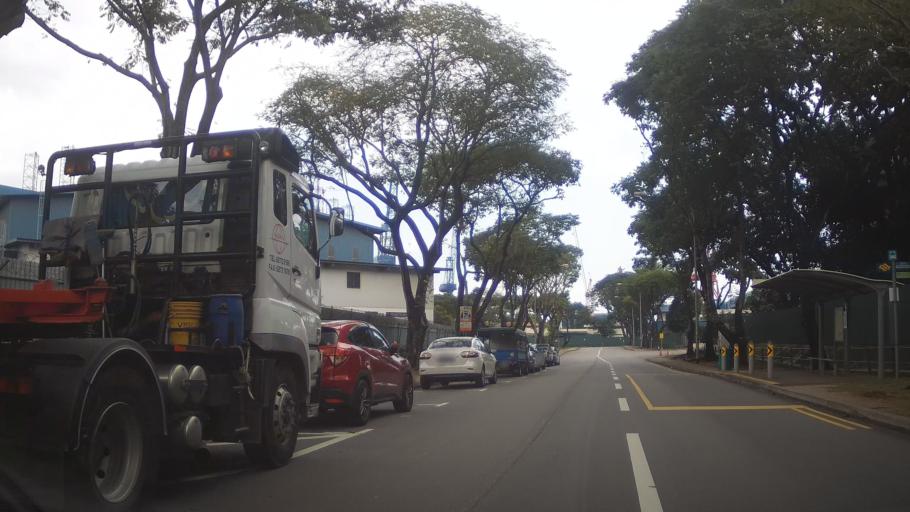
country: SG
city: Singapore
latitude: 1.3019
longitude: 103.6773
